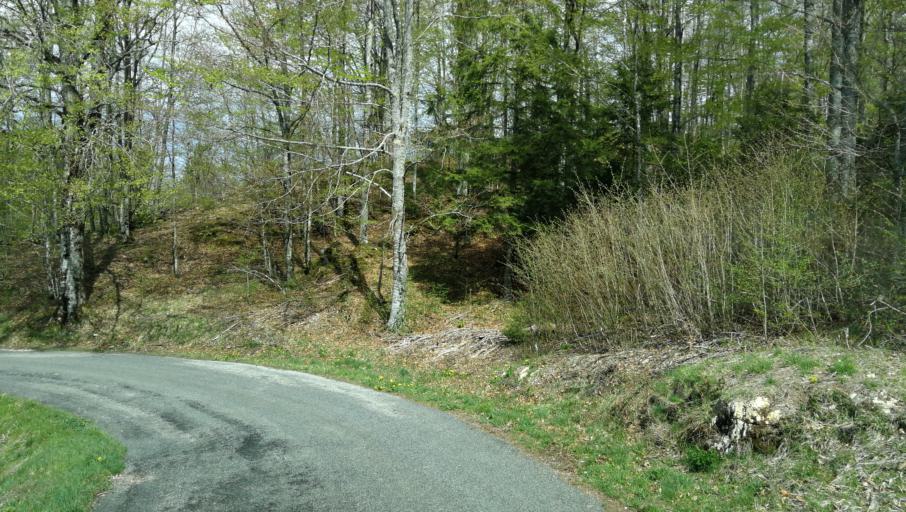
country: FR
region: Rhone-Alpes
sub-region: Departement de l'Ain
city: Chatillon-en-Michaille
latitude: 46.2534
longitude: 5.7919
